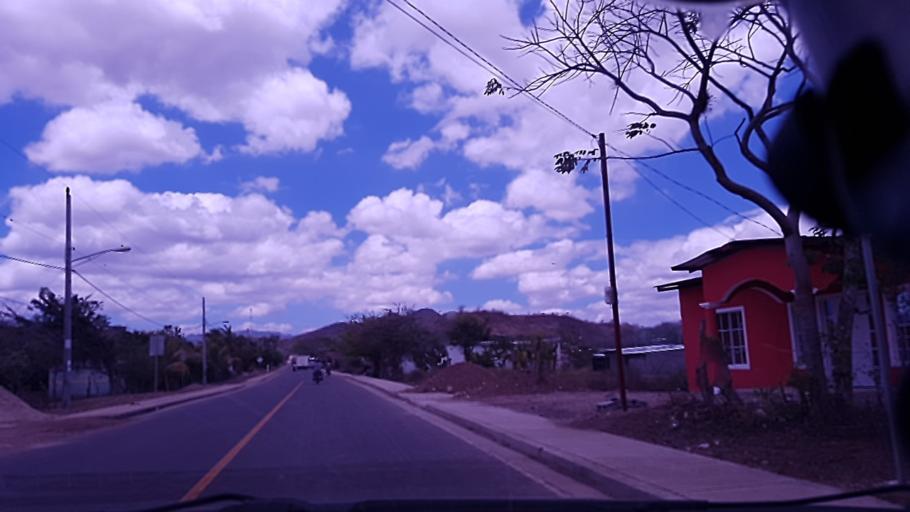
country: NI
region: Esteli
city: Condega
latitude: 13.3769
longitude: -86.3903
